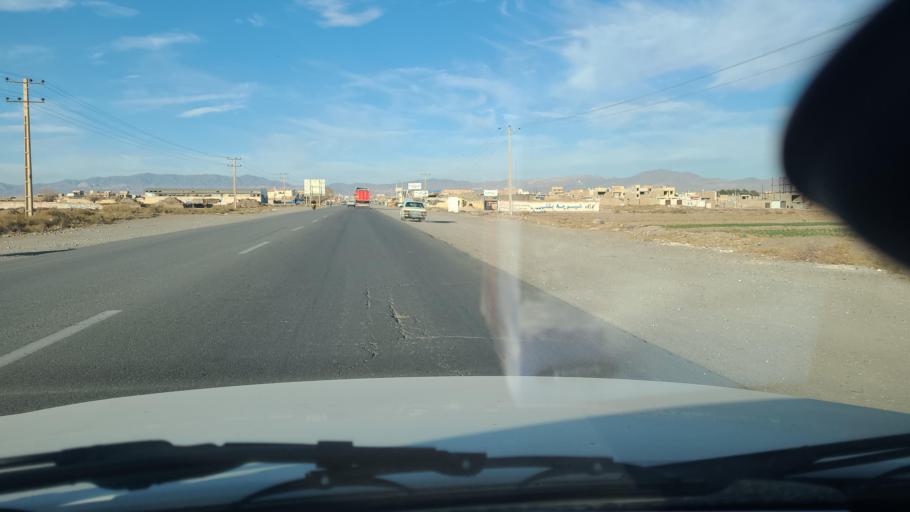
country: IR
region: Razavi Khorasan
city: Sabzevar
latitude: 36.2107
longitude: 57.6505
